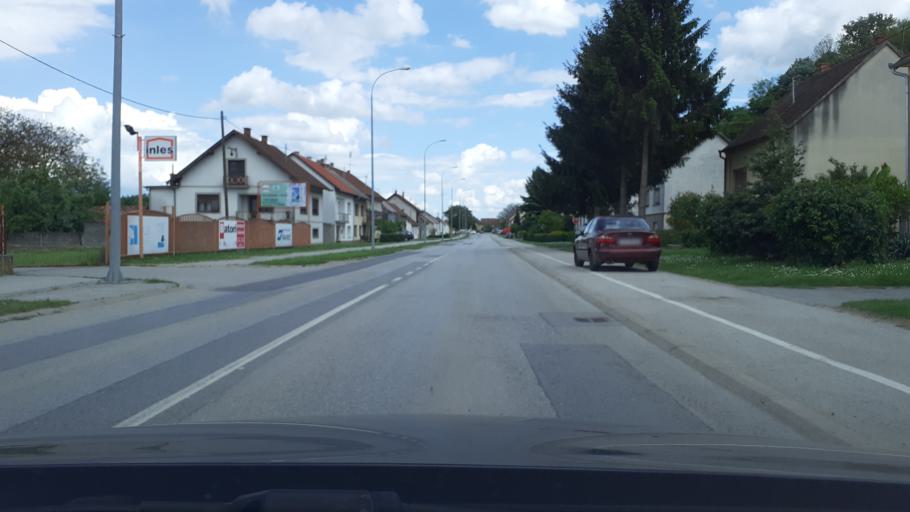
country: HR
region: Pozesko-Slavonska
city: Vidovci
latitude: 45.3342
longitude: 17.7016
